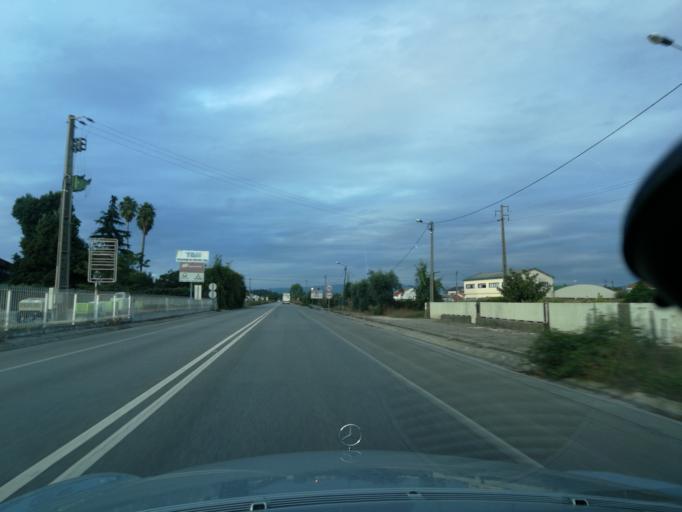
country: PT
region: Aveiro
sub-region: Agueda
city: Valongo
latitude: 40.6134
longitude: -8.4644
